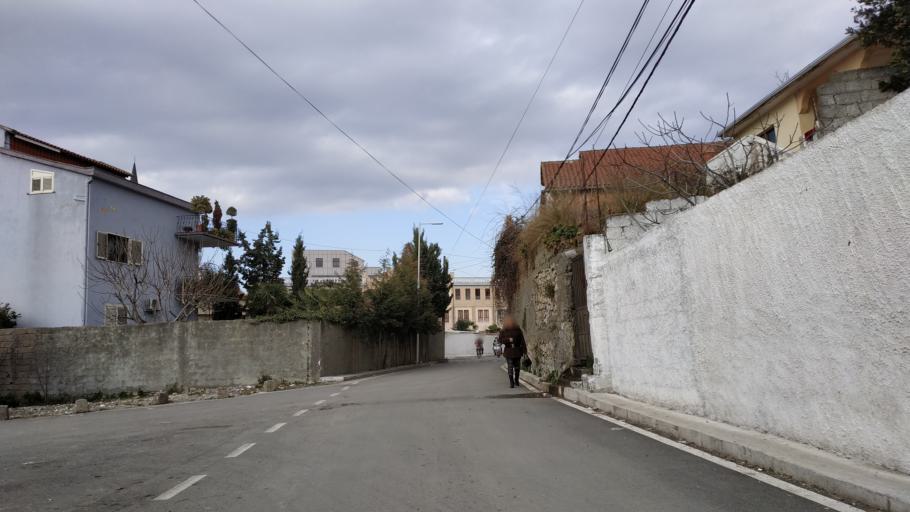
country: AL
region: Shkoder
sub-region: Rrethi i Shkodres
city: Shkoder
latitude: 42.0559
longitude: 19.5030
